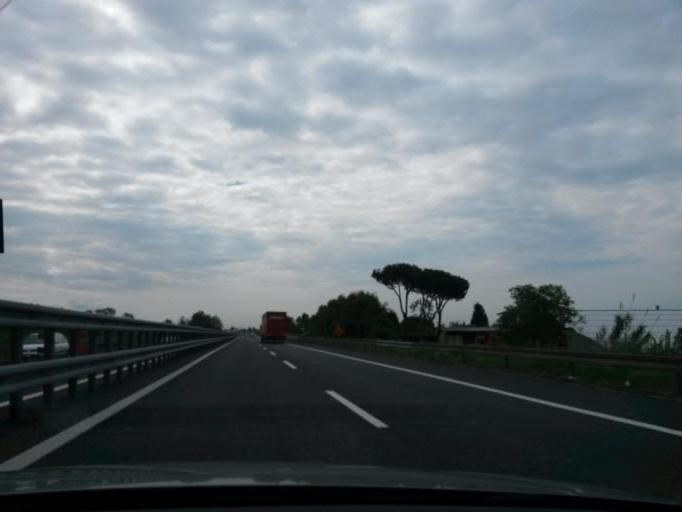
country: IT
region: Tuscany
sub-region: Provincia di Lucca
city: Camaiore
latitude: 43.9151
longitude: 10.2357
